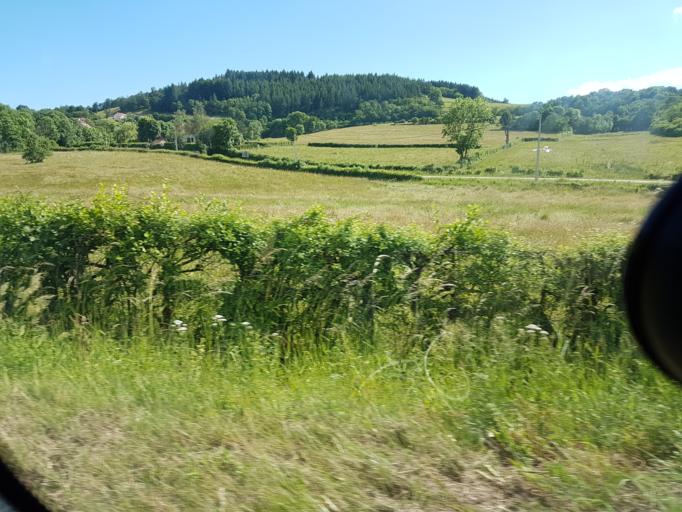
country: FR
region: Bourgogne
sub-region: Departement de Saone-et-Loire
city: Autun
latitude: 47.0593
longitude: 4.2627
